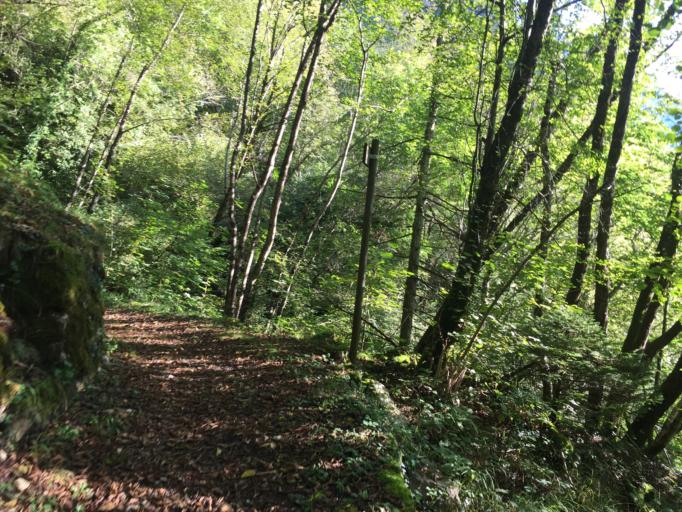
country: IT
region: Friuli Venezia Giulia
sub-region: Provincia di Pordenone
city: Tramonti di Sopra
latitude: 46.3021
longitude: 12.7311
